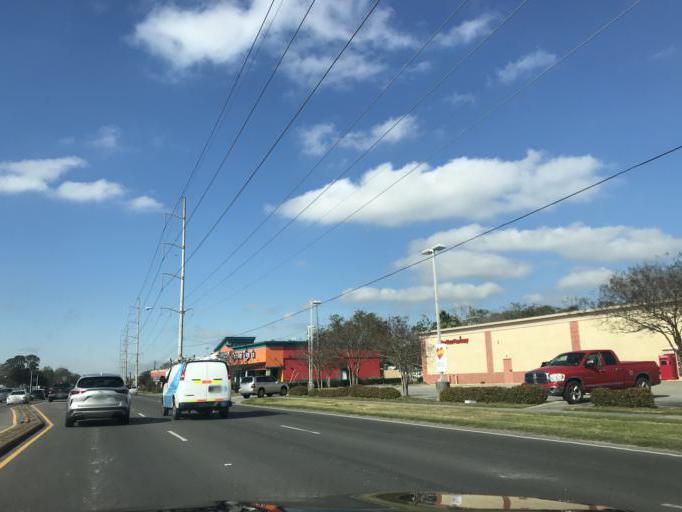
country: US
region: Louisiana
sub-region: Jefferson Parish
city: Metairie Terrace
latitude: 29.9754
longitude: -90.1749
